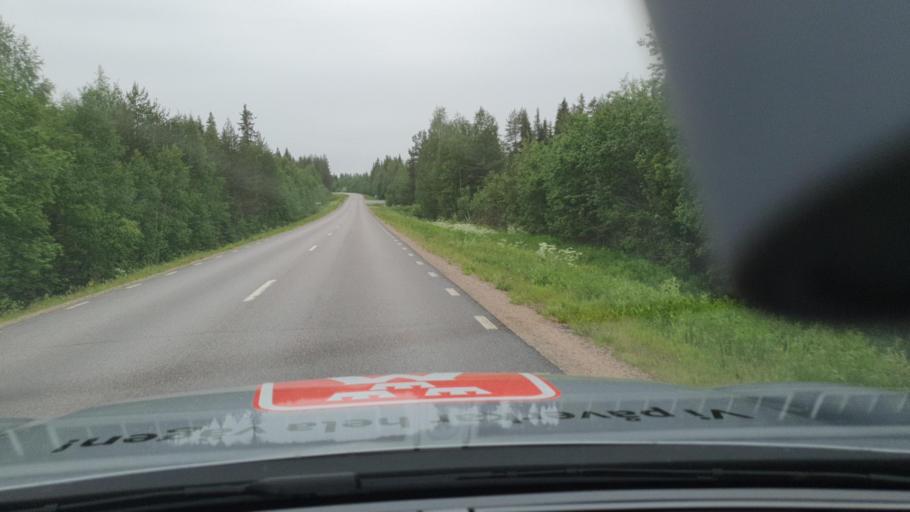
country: SE
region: Norrbotten
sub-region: Overtornea Kommun
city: OEvertornea
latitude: 66.4046
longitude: 23.4804
